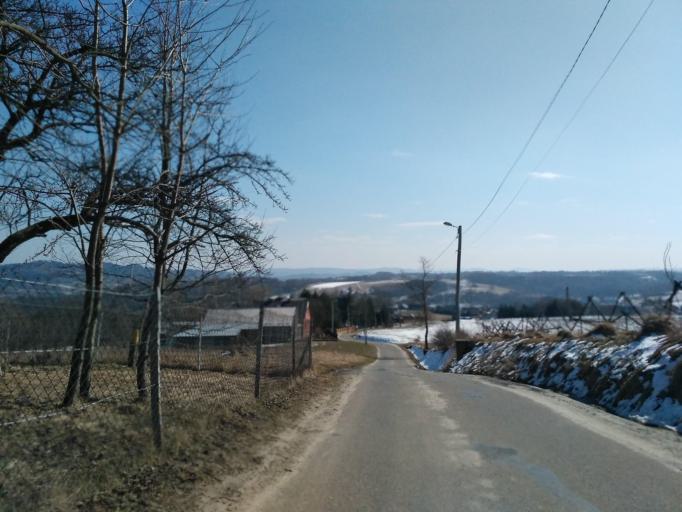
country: PL
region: Subcarpathian Voivodeship
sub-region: Powiat brzozowski
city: Jasienica Rosielna
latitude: 49.7574
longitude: 21.9357
